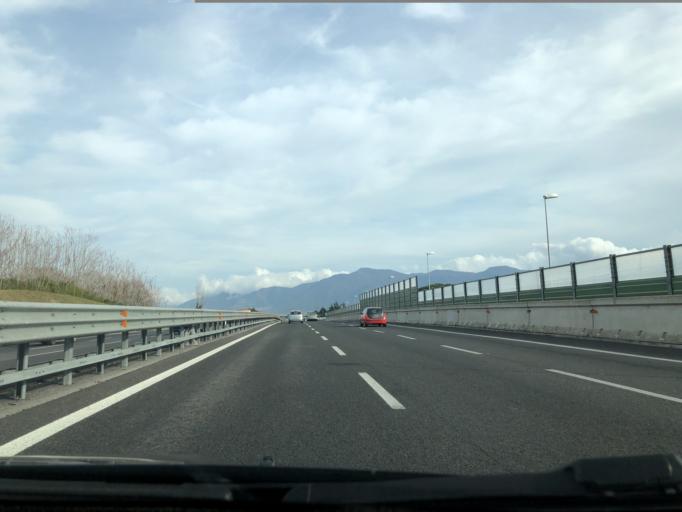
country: IT
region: Campania
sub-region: Provincia di Napoli
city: Trecase
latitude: 40.7692
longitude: 14.4213
